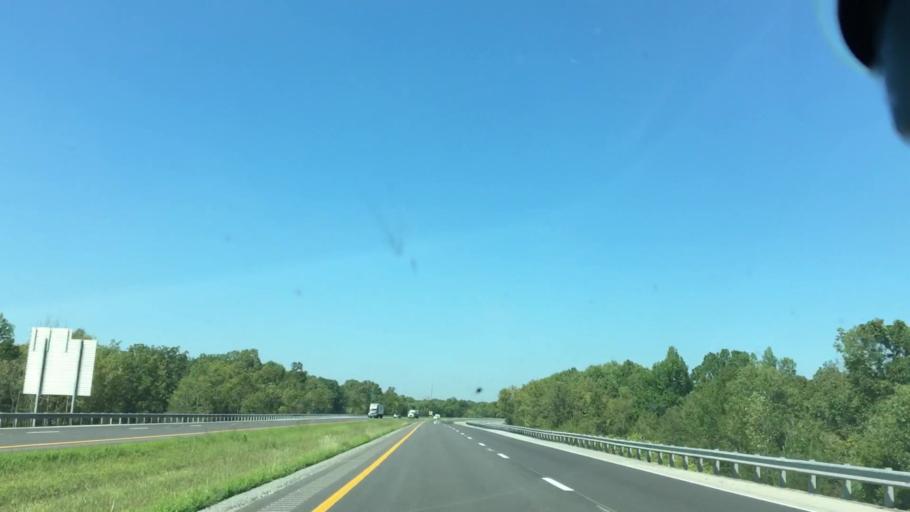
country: US
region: Kentucky
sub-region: Webster County
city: Sebree
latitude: 37.6209
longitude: -87.5046
